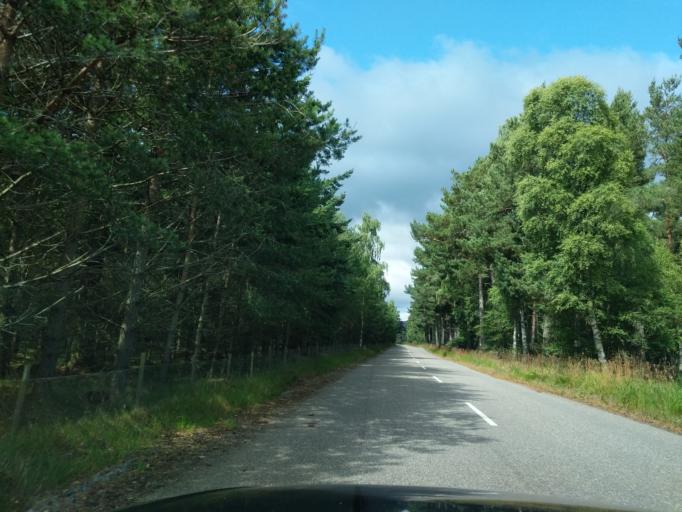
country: GB
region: Scotland
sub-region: Aberdeenshire
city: Aboyne
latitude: 57.0705
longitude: -2.8596
